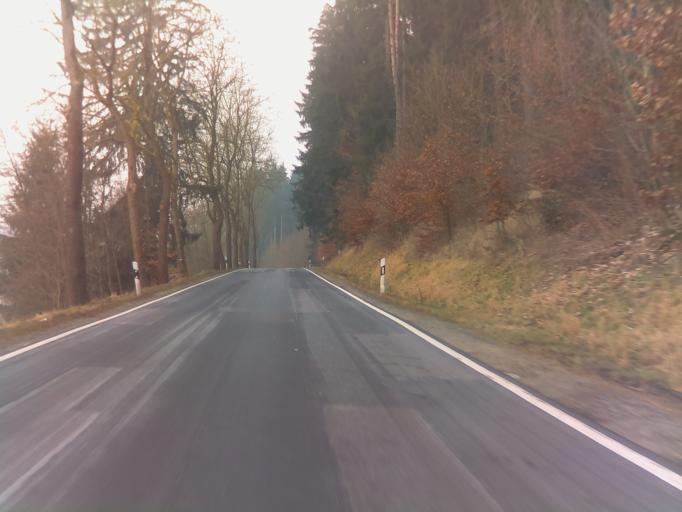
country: DE
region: Thuringia
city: Schwarza
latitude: 50.6358
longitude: 10.5456
